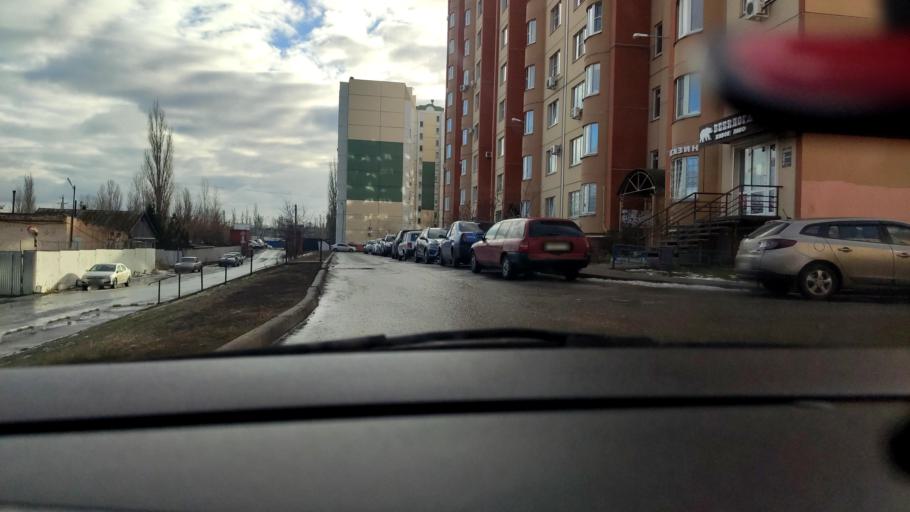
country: RU
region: Voronezj
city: Pridonskoy
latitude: 51.6226
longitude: 39.0645
